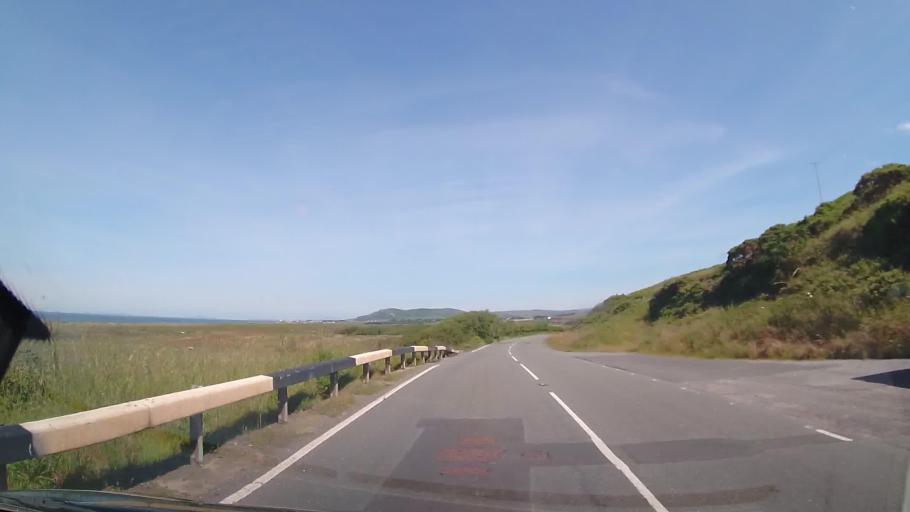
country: GB
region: Wales
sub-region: Gwynedd
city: Tywyn
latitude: 52.5558
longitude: -4.0720
